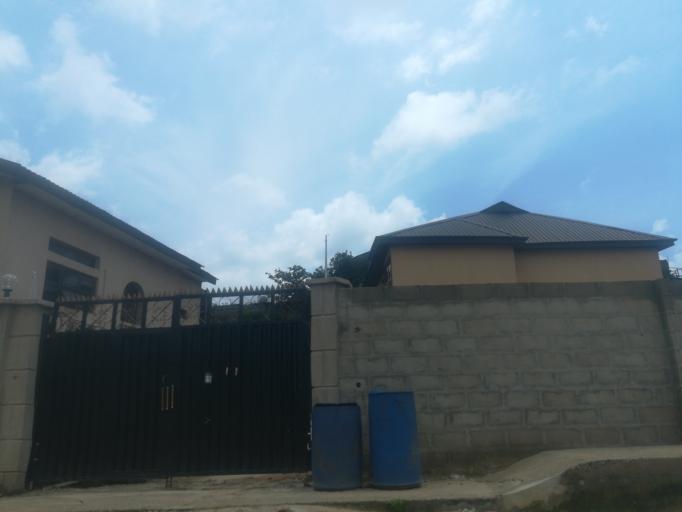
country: NG
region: Lagos
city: Ojota
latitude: 6.5646
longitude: 3.3913
